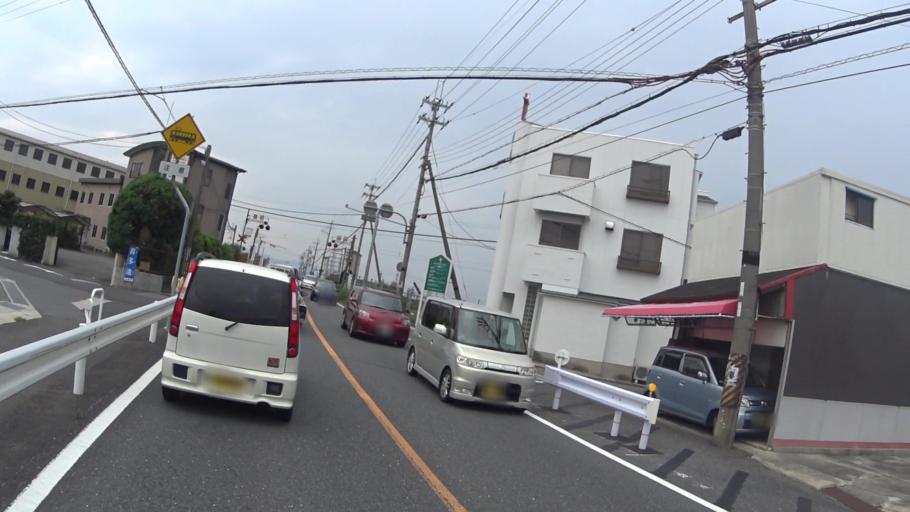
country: JP
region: Kyoto
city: Tanabe
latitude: 34.8247
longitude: 135.7609
